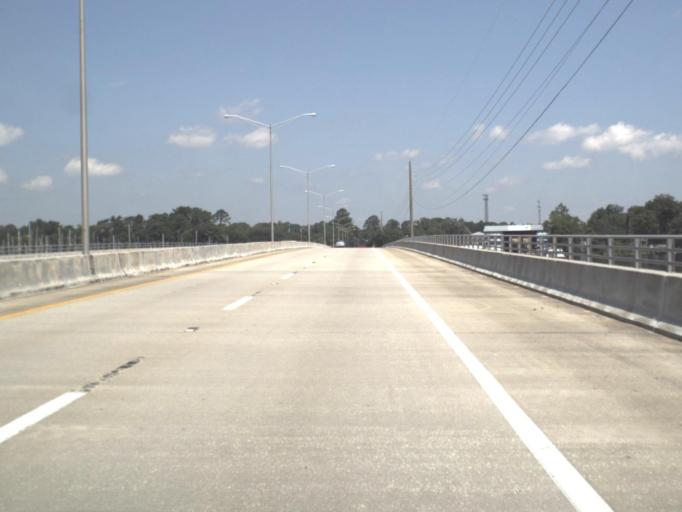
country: US
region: Florida
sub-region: Saint Johns County
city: Fruit Cove
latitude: 30.1304
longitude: -81.6280
